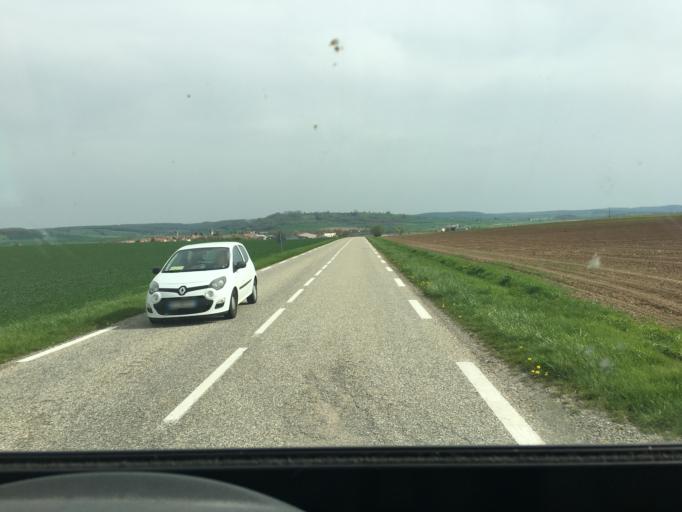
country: FR
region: Lorraine
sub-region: Departement de la Moselle
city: Vic-sur-Seille
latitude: 48.7652
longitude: 6.5576
